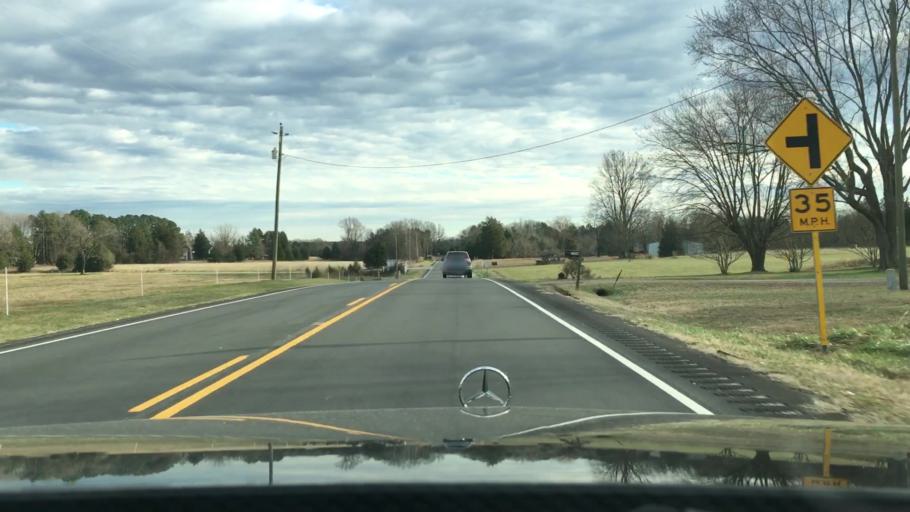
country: US
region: North Carolina
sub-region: Caswell County
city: Yanceyville
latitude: 36.3694
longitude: -79.2566
